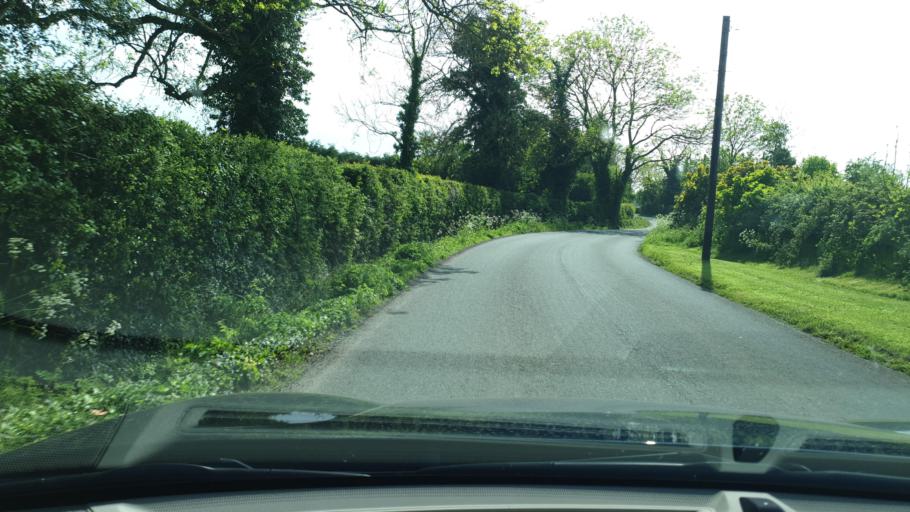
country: IE
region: Leinster
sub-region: Kildare
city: Maynooth
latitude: 53.4121
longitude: -6.5741
